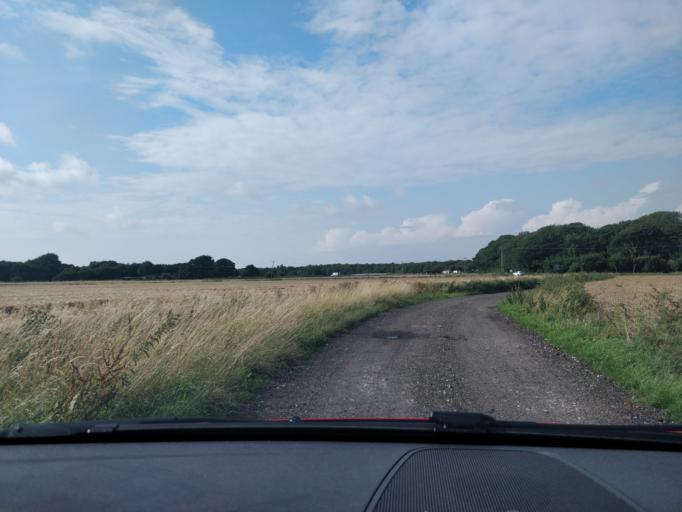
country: GB
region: England
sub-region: Lancashire
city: Banks
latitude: 53.6492
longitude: -2.9488
